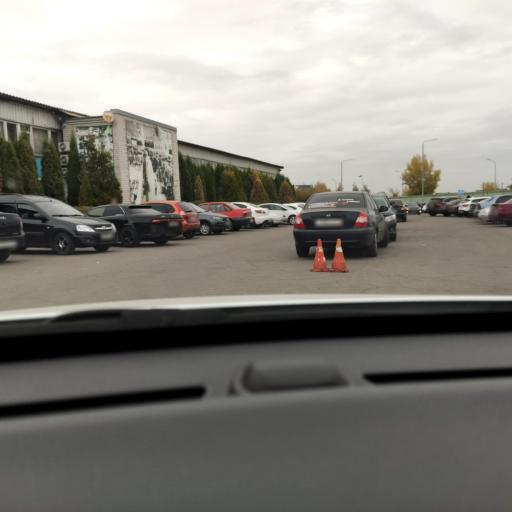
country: RU
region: Voronezj
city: Somovo
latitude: 51.6798
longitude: 39.3004
